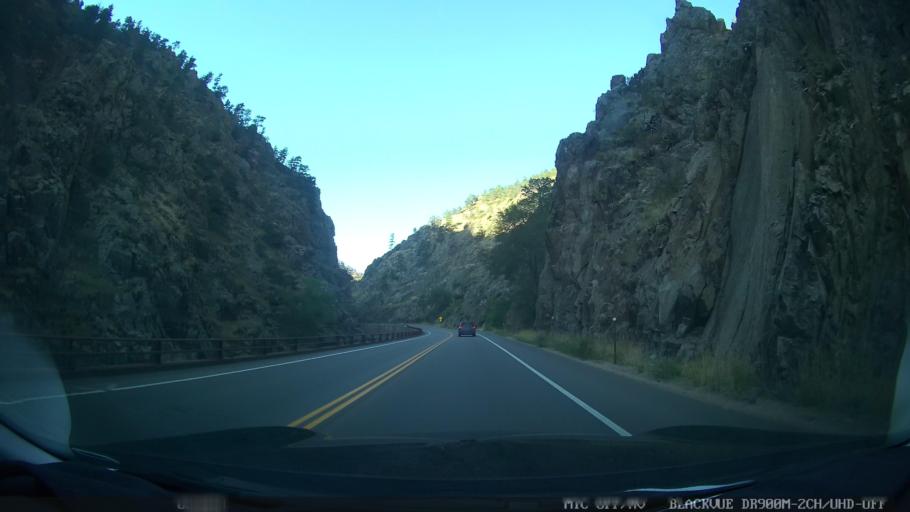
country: US
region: Colorado
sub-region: Larimer County
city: Loveland
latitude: 40.4209
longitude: -105.2422
